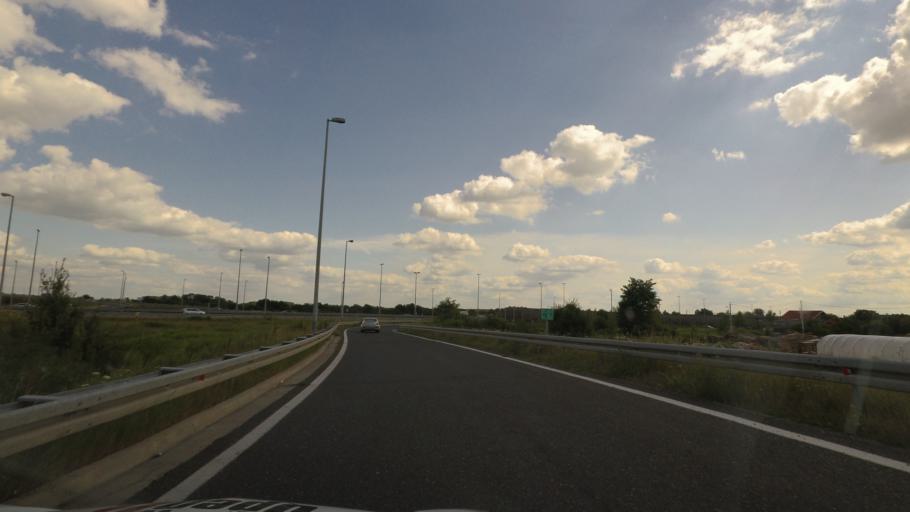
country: HR
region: Zagrebacka
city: Micevec
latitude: 45.7640
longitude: 16.0878
